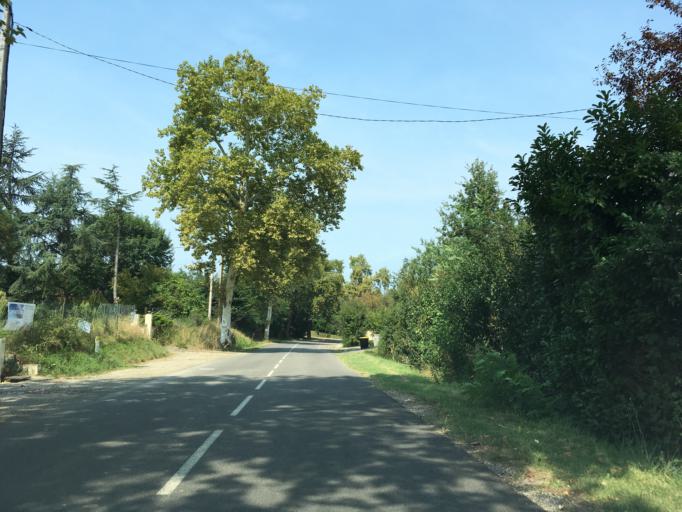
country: FR
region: Midi-Pyrenees
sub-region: Departement du Tarn-et-Garonne
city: Saint-Nauphary
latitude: 43.9846
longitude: 1.3894
